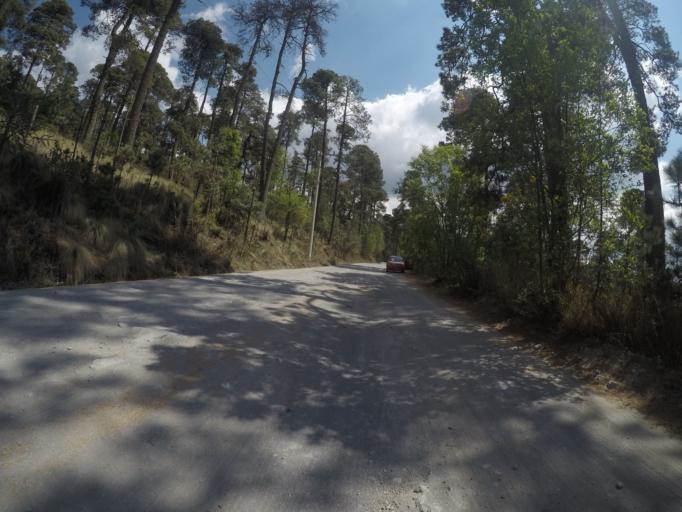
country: MX
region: Mexico
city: Cerro La Calera
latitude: 19.1502
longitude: -99.8032
